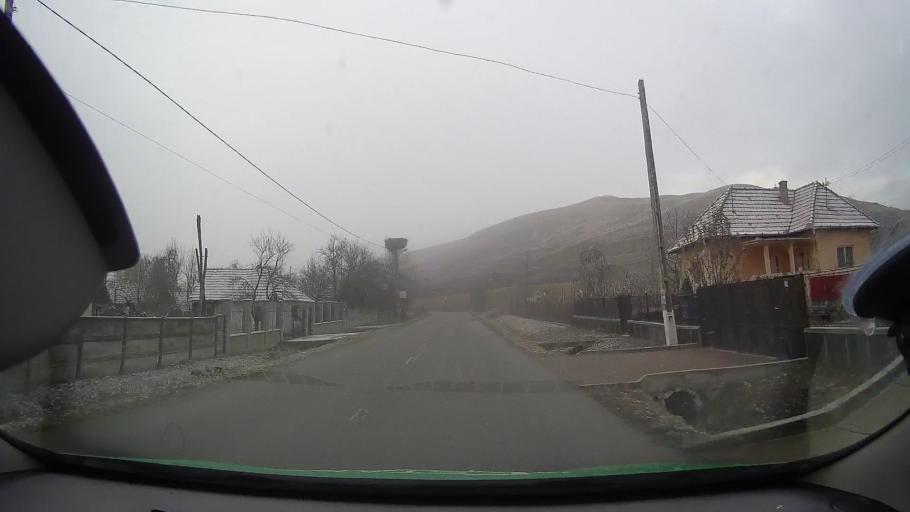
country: RO
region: Alba
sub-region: Comuna Noslac
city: Noslac
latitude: 46.3667
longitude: 23.9312
